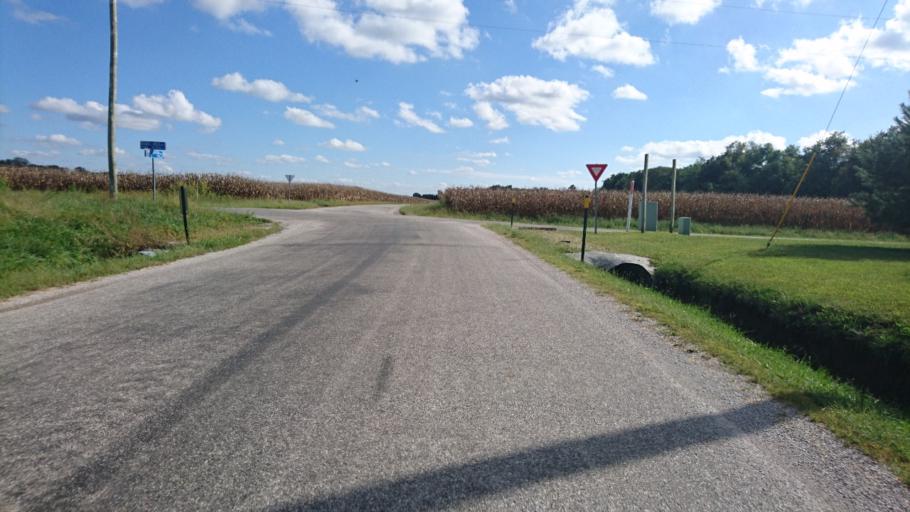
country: US
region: Illinois
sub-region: Macoupin County
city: Staunton
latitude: 39.0028
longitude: -89.7314
